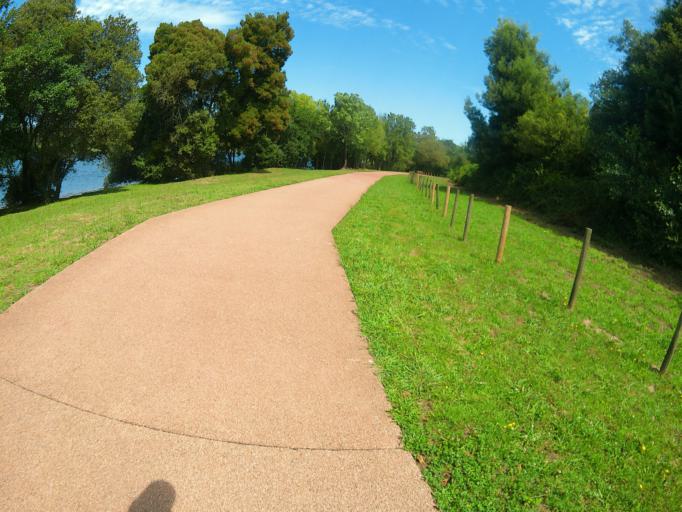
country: PT
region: Viana do Castelo
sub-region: Vila Nova de Cerveira
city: Vila Nova de Cerveira
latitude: 41.9344
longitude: -8.7522
